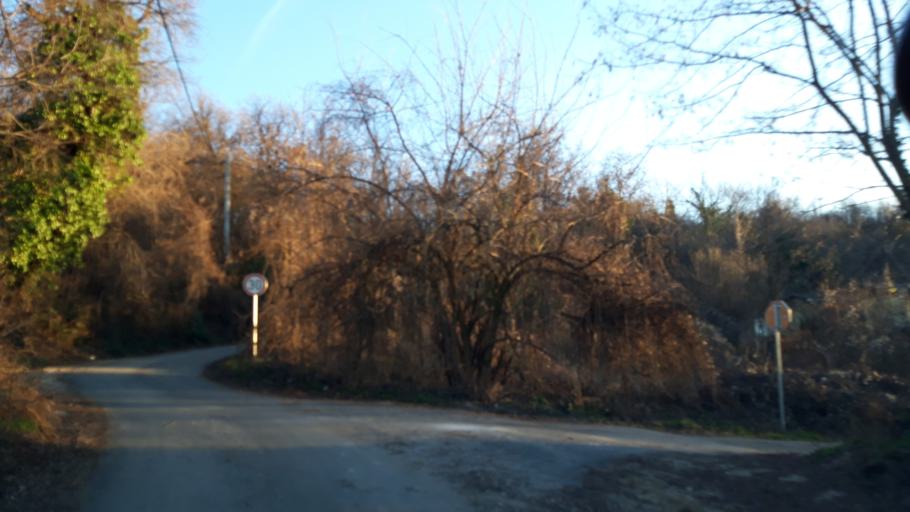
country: RS
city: Cortanovci
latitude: 45.1663
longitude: 19.9991
